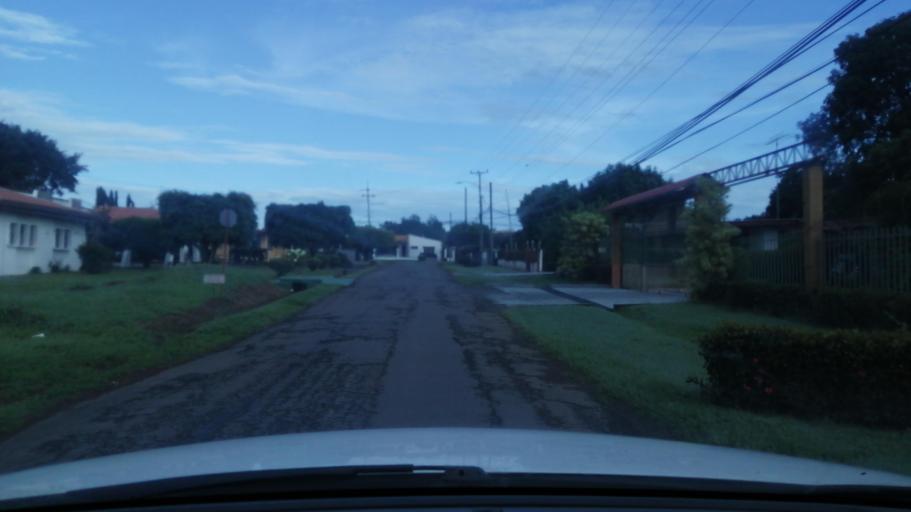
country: PA
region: Chiriqui
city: El Quiteno
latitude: 8.4586
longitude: -82.4172
